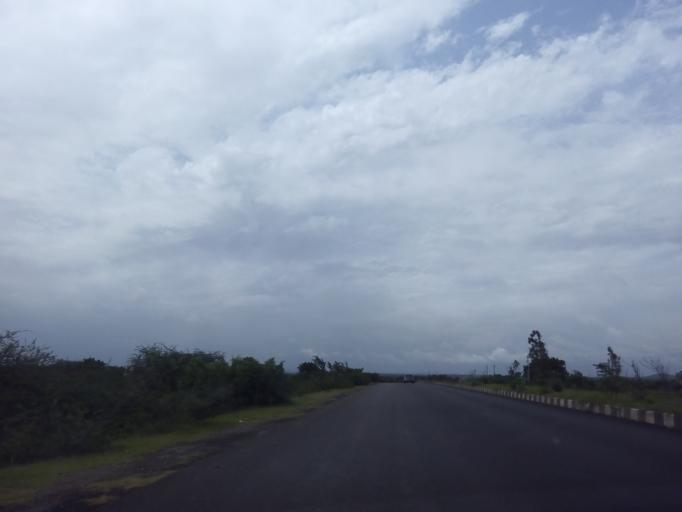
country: IN
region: Karnataka
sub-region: Haveri
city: Byadgi
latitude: 14.7032
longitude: 75.5203
